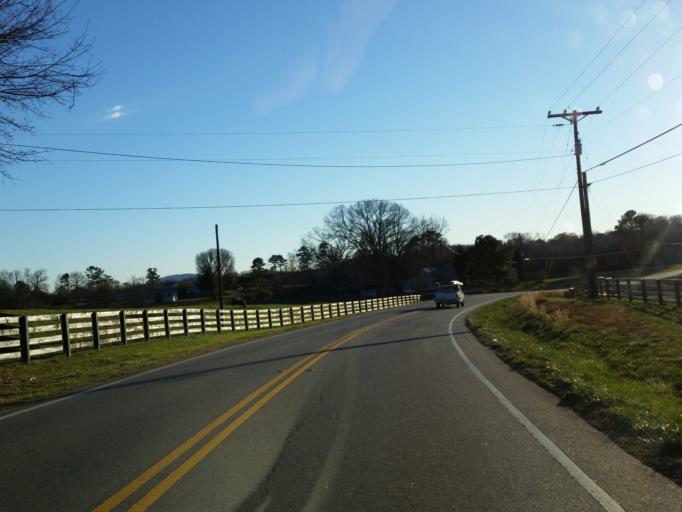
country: US
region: Georgia
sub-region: Cherokee County
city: Holly Springs
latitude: 34.1584
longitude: -84.4284
